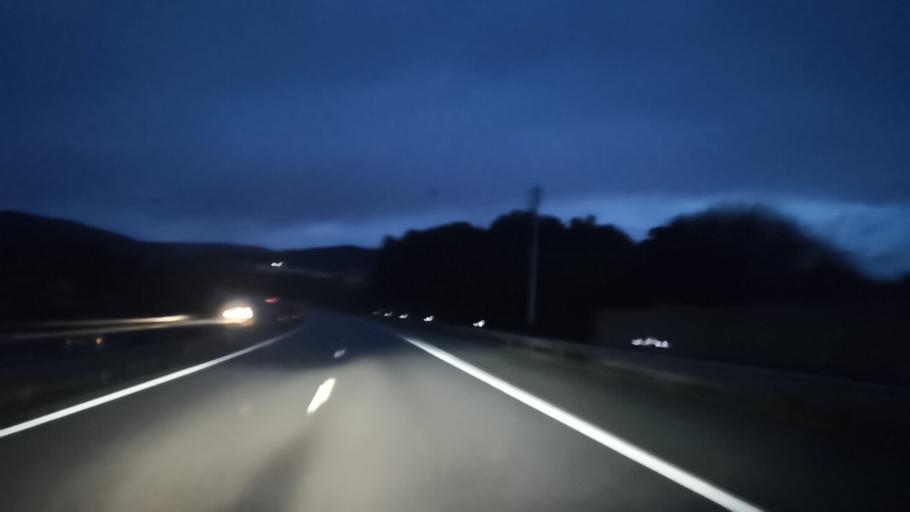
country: PT
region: Braga
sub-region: Guimaraes
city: Ponte
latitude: 41.4532
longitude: -8.3385
